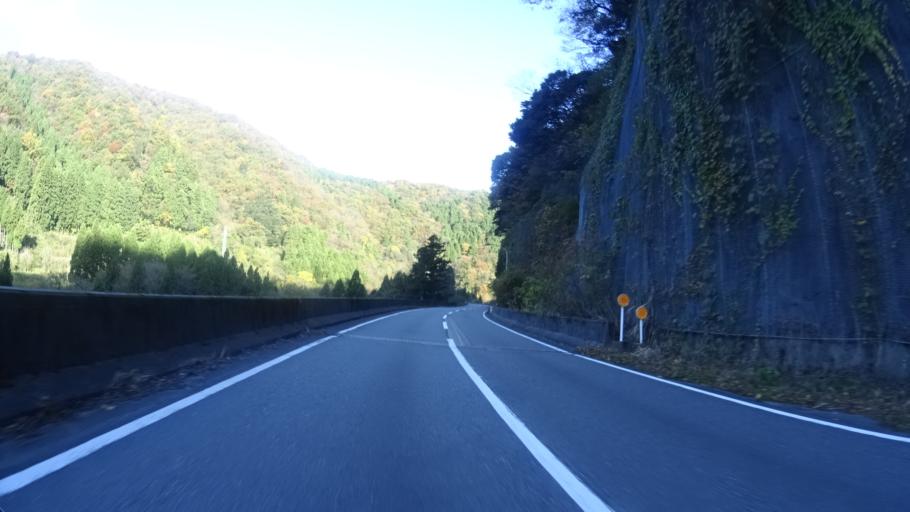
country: JP
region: Fukui
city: Maruoka
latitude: 36.2168
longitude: 136.3526
